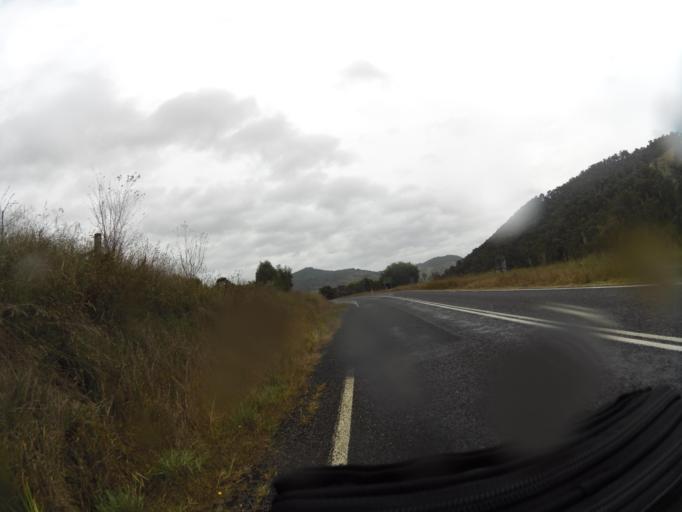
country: AU
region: New South Wales
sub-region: Greater Hume Shire
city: Holbrook
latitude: -36.2229
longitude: 147.6647
